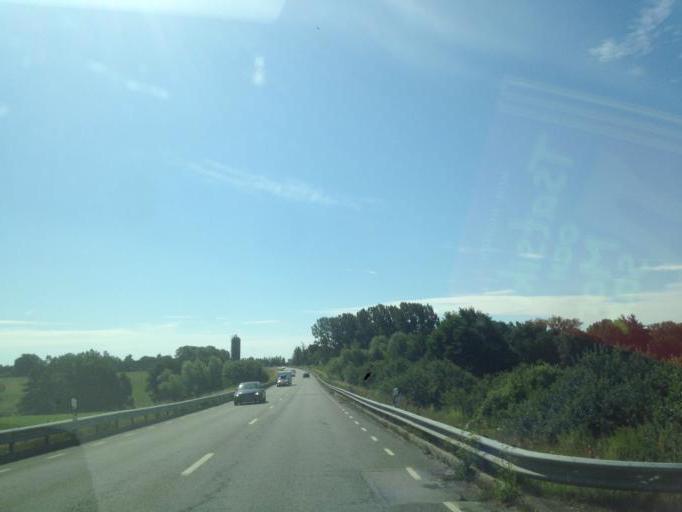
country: SE
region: Skane
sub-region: Simrishamns Kommun
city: Kivik
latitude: 55.6287
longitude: 14.2553
